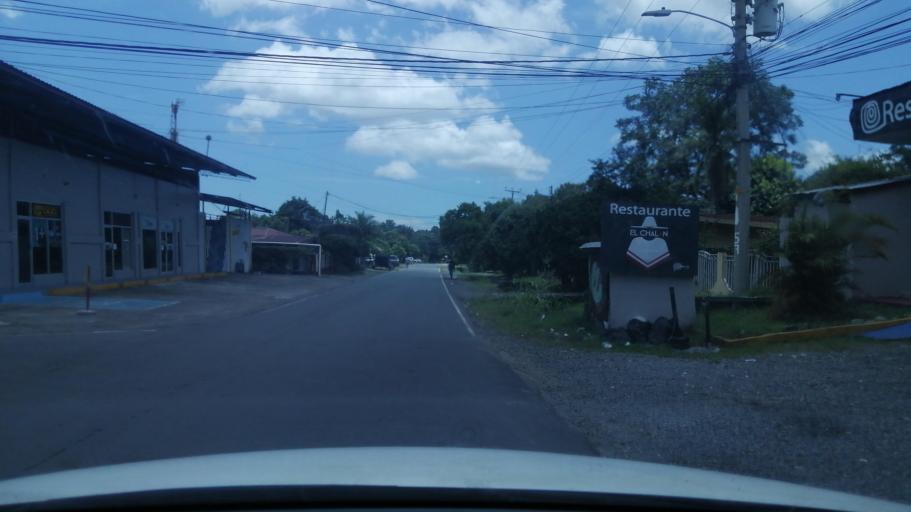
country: PA
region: Chiriqui
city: David
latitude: 8.4266
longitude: -82.4372
